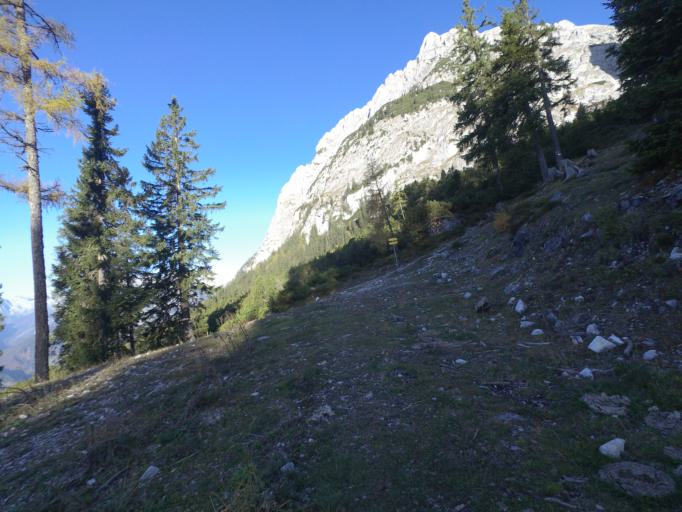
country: AT
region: Salzburg
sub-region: Politischer Bezirk Sankt Johann im Pongau
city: Werfenweng
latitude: 47.4869
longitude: 13.2292
